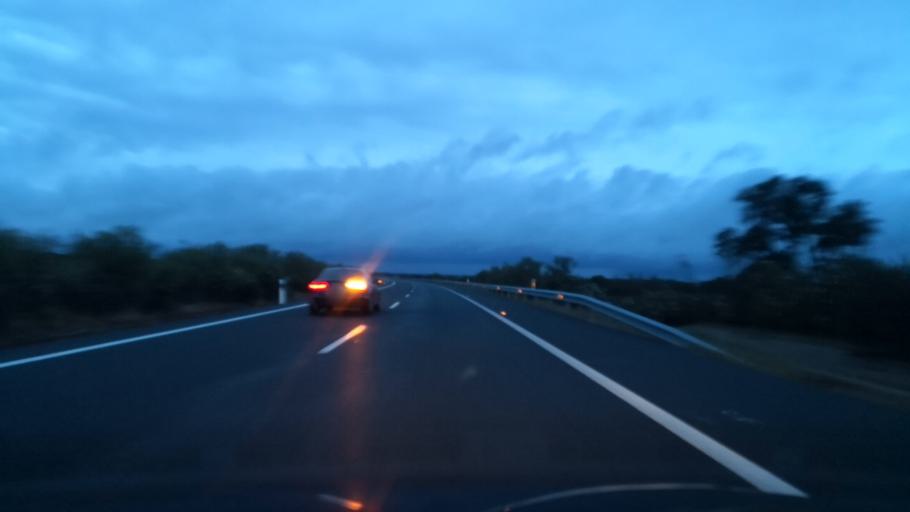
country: ES
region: Extremadura
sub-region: Provincia de Caceres
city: Casas de Don Antonio
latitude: 39.2130
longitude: -6.2872
